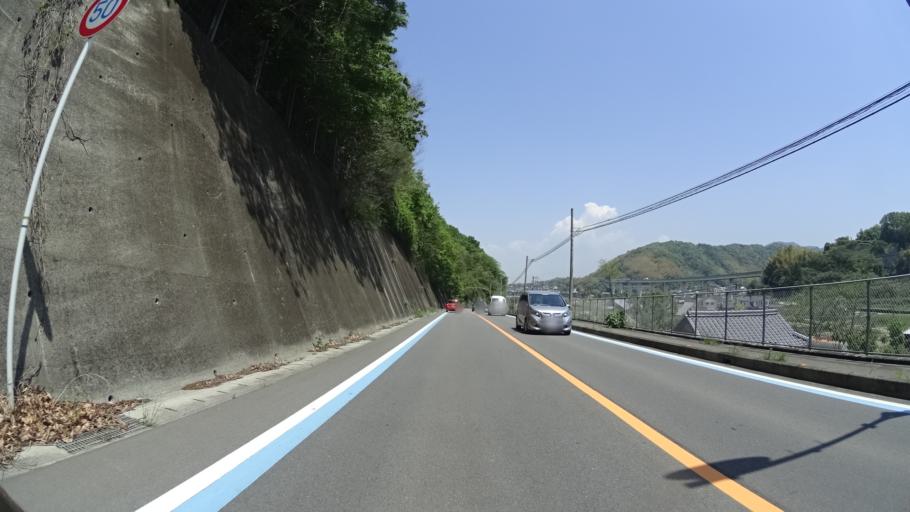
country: JP
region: Ehime
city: Iyo
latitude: 33.7288
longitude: 132.6890
